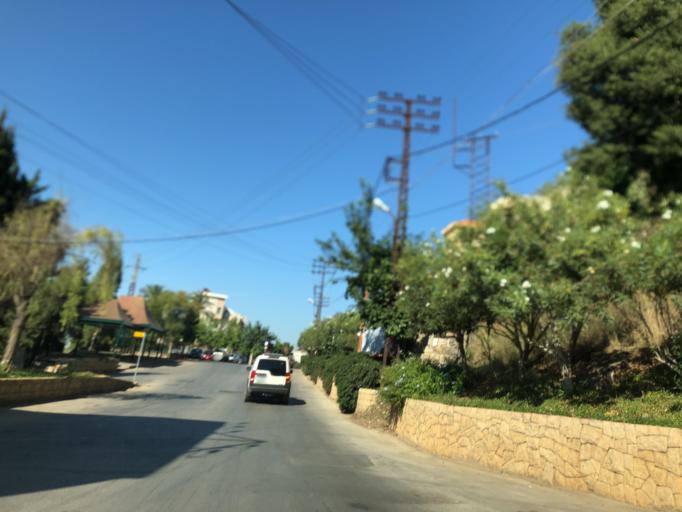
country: LB
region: Mont-Liban
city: Jdaidet el Matn
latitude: 33.8830
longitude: 35.6331
